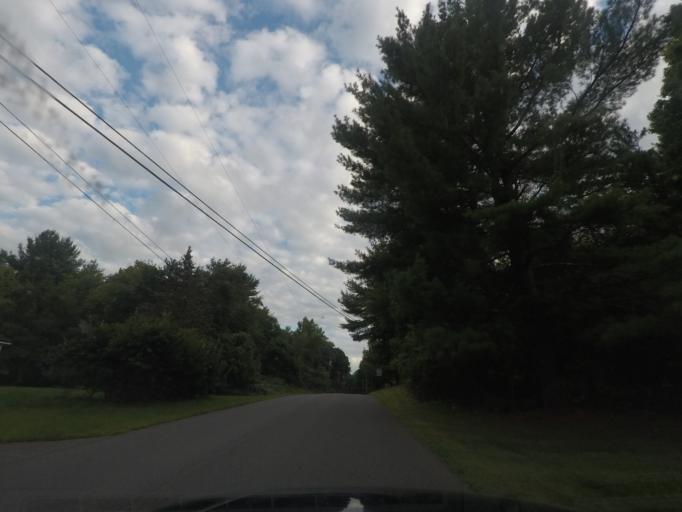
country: US
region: New York
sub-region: Rensselaer County
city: Nassau
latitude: 42.5079
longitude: -73.6080
